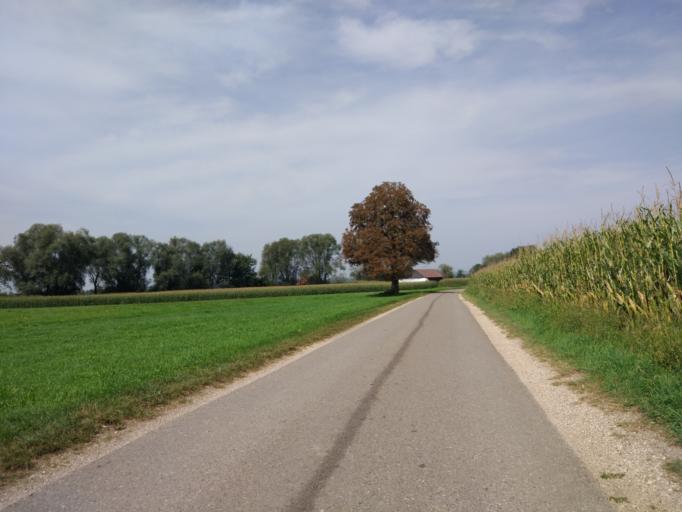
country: DE
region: Baden-Wuerttemberg
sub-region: Tuebingen Region
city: Achstetten
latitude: 48.2823
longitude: 9.8983
